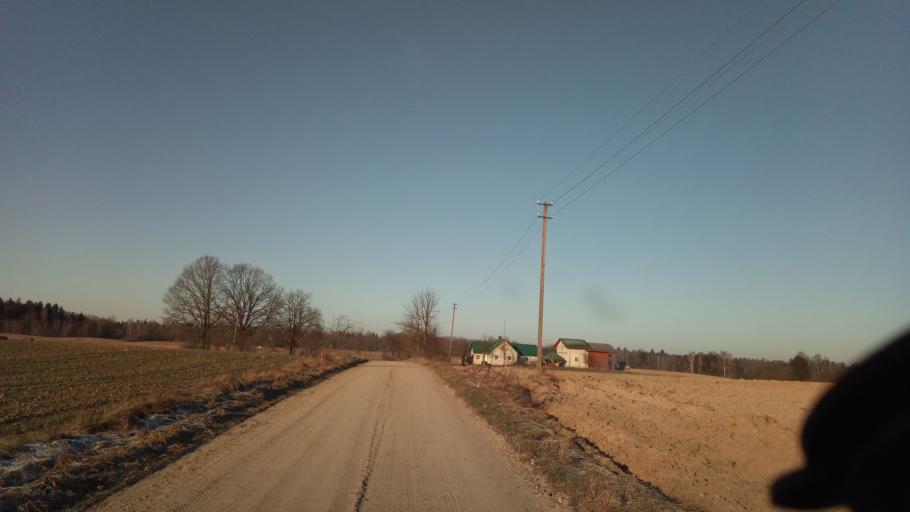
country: LT
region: Alytaus apskritis
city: Druskininkai
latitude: 54.1004
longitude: 24.0107
